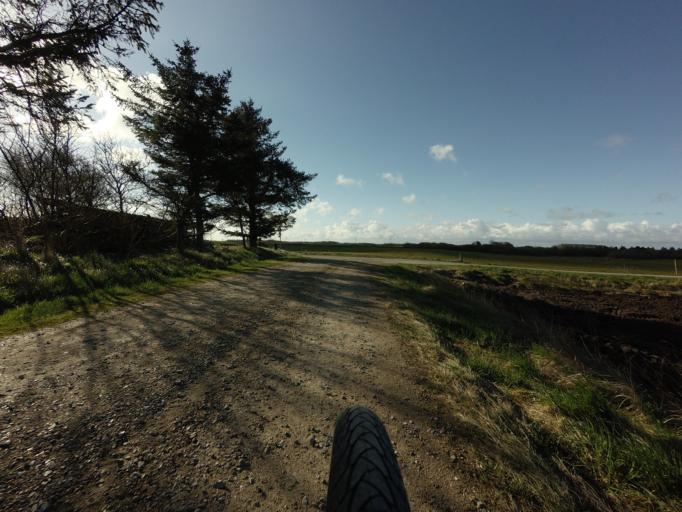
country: DK
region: North Denmark
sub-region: Hjorring Kommune
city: Vra
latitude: 57.3605
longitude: 9.8176
